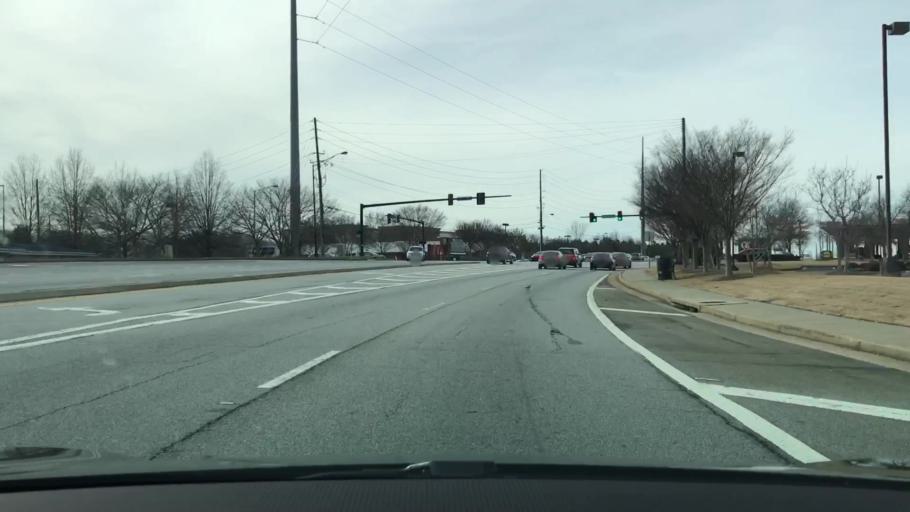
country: US
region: Georgia
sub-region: Gwinnett County
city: Suwanee
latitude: 34.0003
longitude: -84.0682
